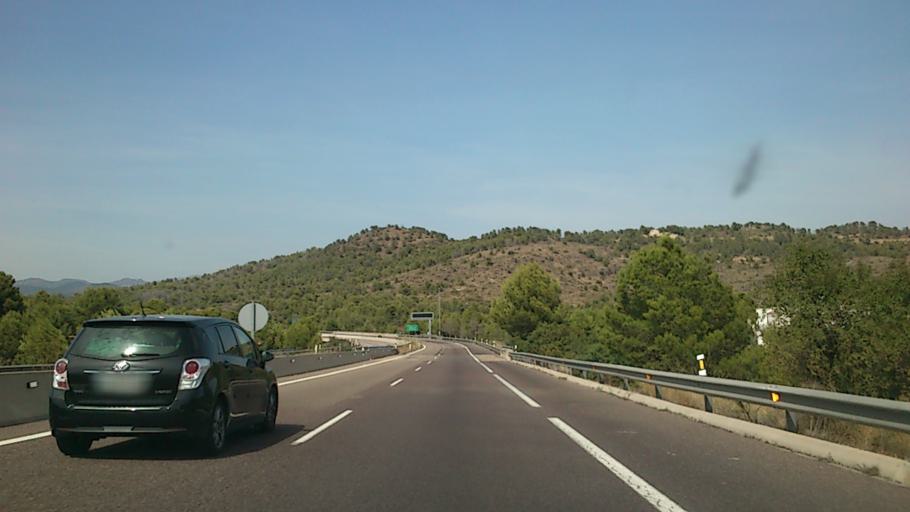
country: ES
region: Valencia
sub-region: Provincia de Valencia
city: Algimia de Alfara
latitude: 39.7650
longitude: -0.3901
